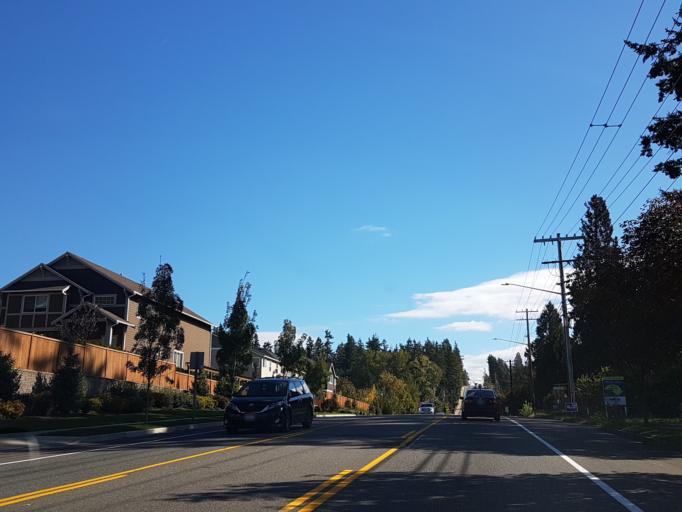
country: US
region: Washington
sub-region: Snohomish County
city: North Creek
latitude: 47.7911
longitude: -122.1843
